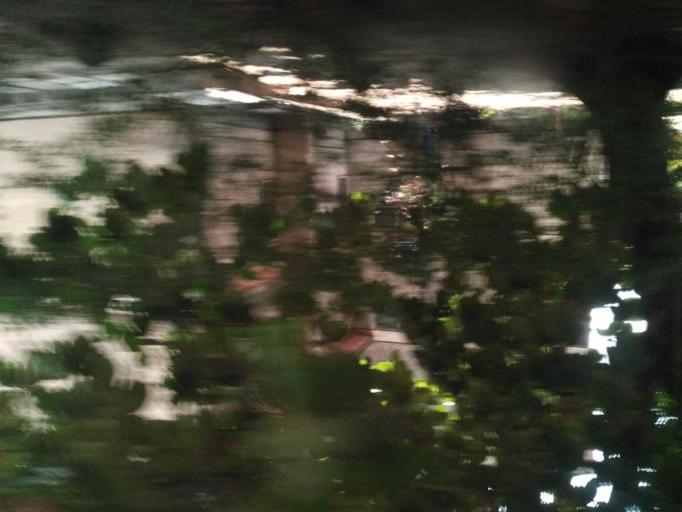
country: TZ
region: Dar es Salaam
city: Dar es Salaam
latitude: -6.8086
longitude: 39.2726
